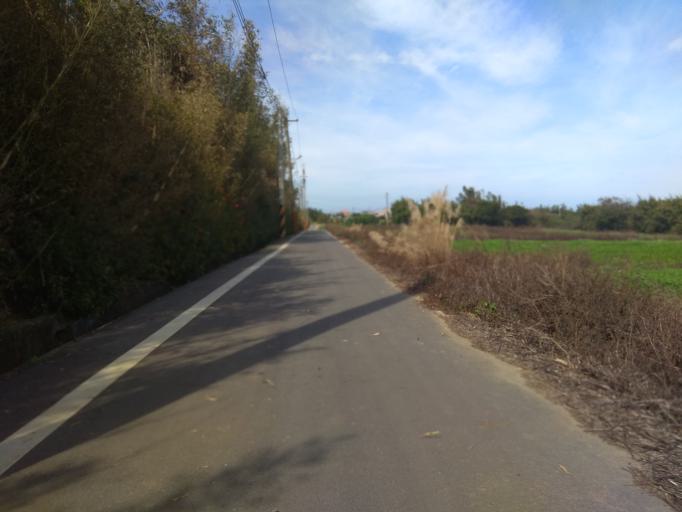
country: TW
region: Taiwan
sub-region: Hsinchu
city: Zhubei
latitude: 25.0131
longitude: 121.0779
